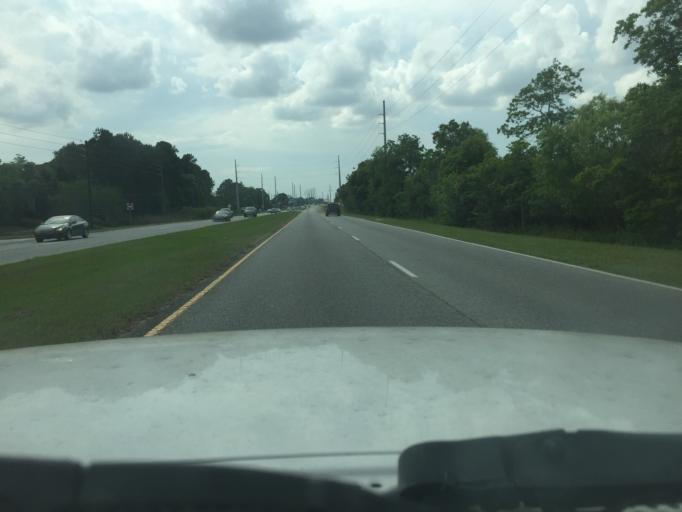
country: US
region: Georgia
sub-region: Chatham County
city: Thunderbolt
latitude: 32.0651
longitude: -81.0373
